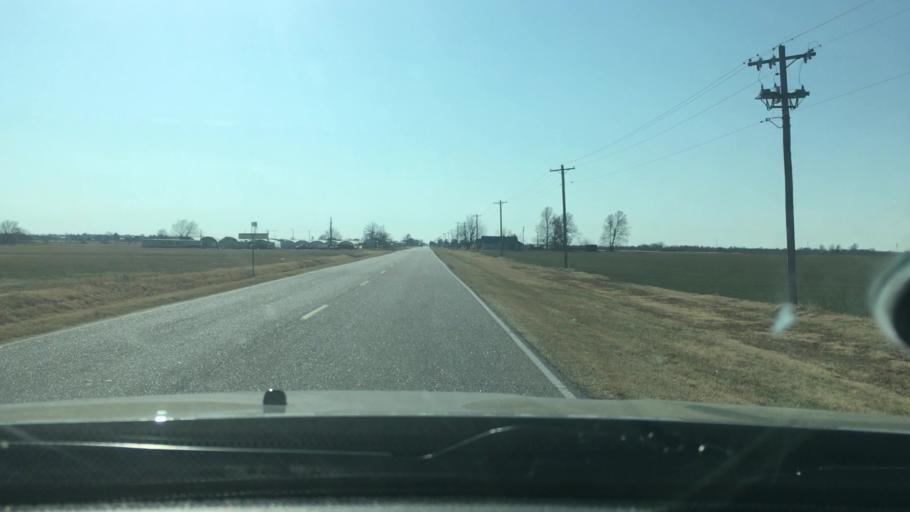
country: US
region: Oklahoma
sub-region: Garvin County
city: Stratford
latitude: 34.8251
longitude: -96.9677
